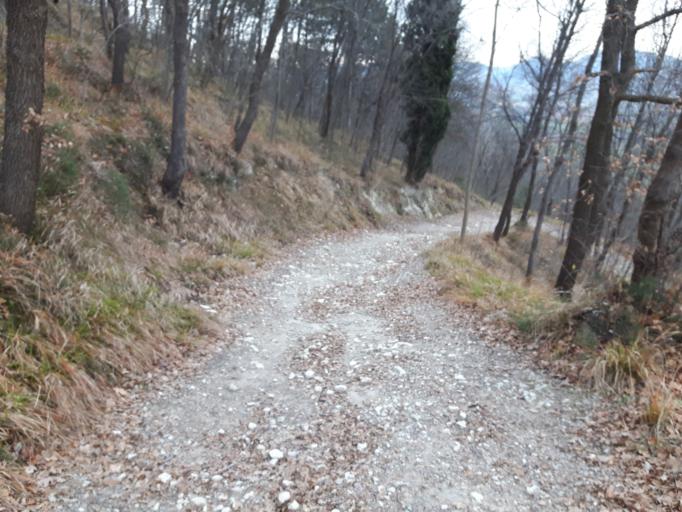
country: IT
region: Veneto
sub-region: Provincia di Padova
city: Arqua Petrarca
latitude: 45.2744
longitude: 11.7418
